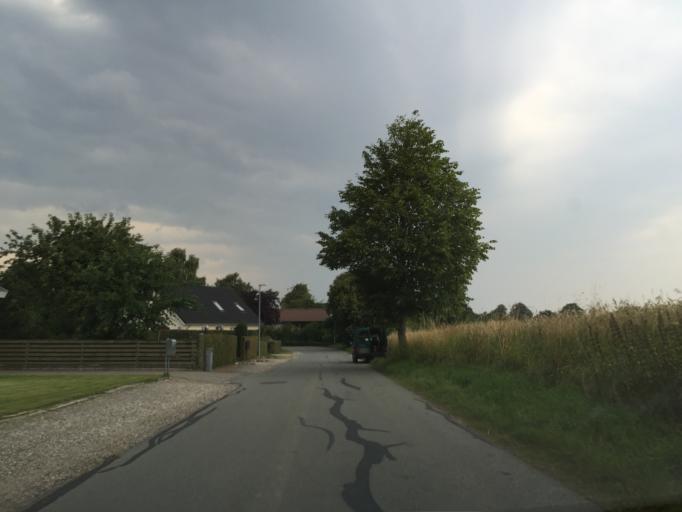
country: DK
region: Central Jutland
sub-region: Viborg Kommune
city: Bjerringbro
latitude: 56.3357
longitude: 9.6413
